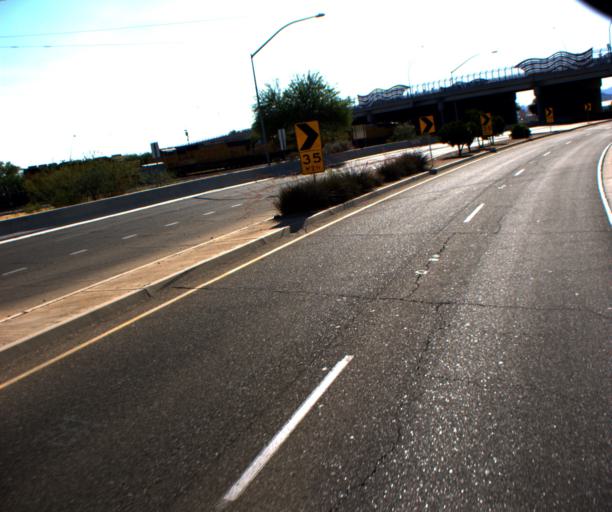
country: US
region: Arizona
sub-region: Pima County
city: Tucson
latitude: 32.1903
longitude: -110.9142
